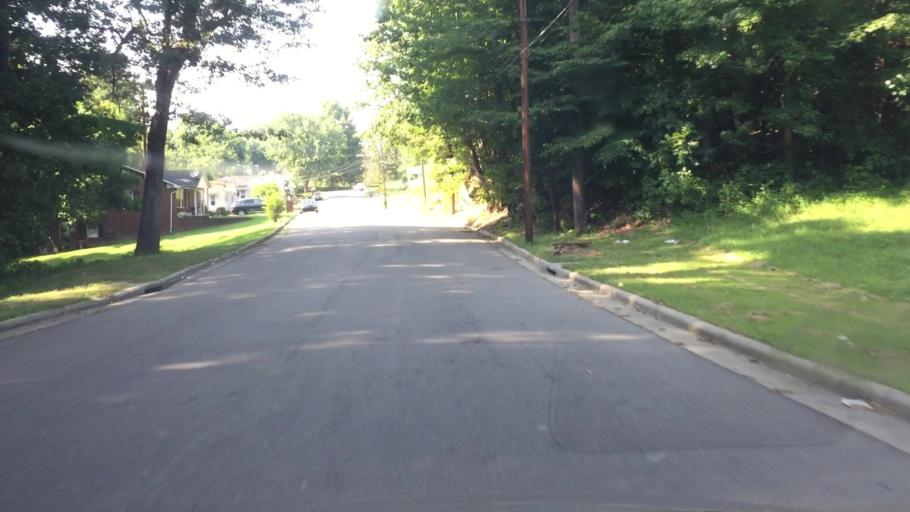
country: US
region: North Carolina
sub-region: Rockingham County
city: Reidsville
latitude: 36.3664
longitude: -79.6713
